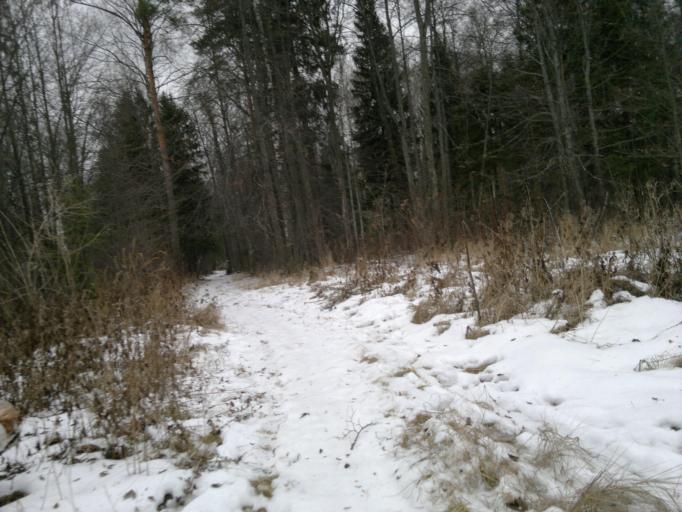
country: RU
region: Mariy-El
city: Yoshkar-Ola
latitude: 56.6099
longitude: 47.9551
